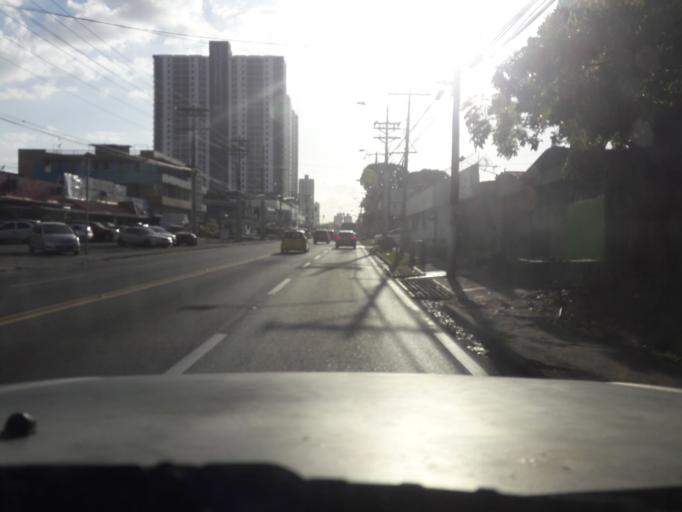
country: PA
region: Panama
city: Panama
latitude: 9.0181
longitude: -79.4936
